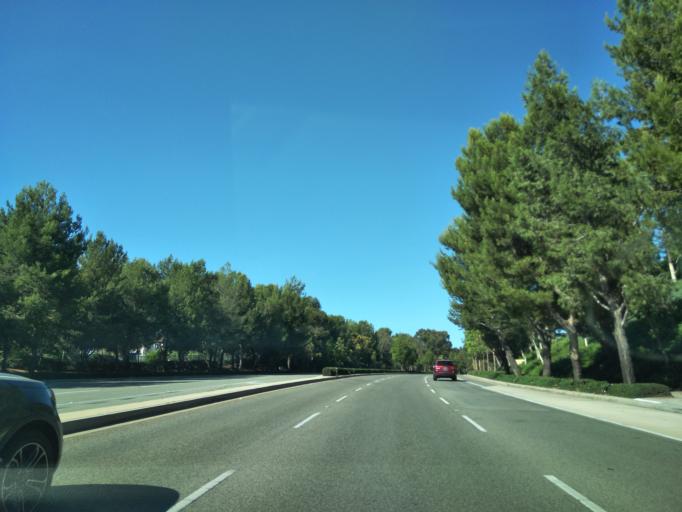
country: US
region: California
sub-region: Orange County
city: San Joaquin Hills
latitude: 33.5961
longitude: -117.8353
